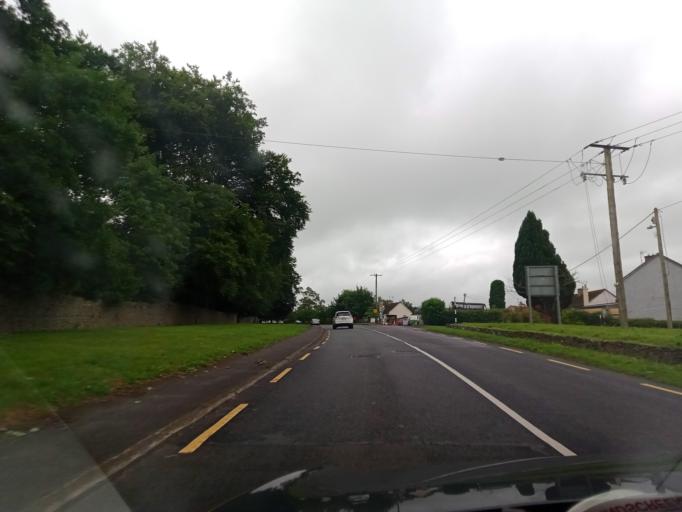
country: IE
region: Leinster
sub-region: Laois
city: Abbeyleix
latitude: 52.9110
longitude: -7.3367
